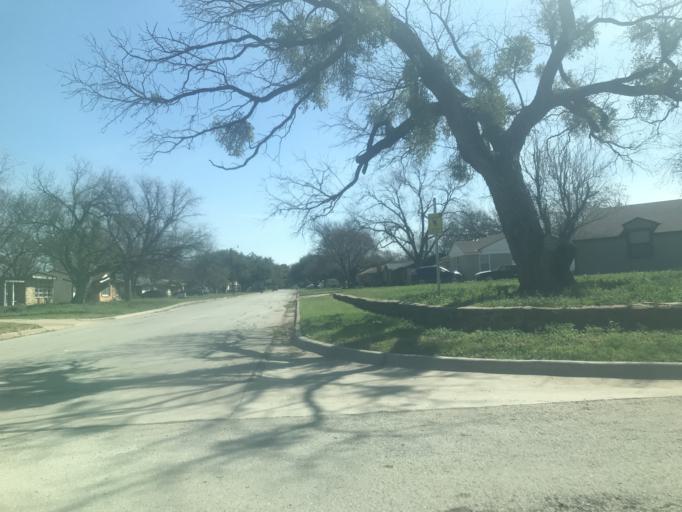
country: US
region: Texas
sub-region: Taylor County
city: Abilene
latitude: 32.4421
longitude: -99.7744
